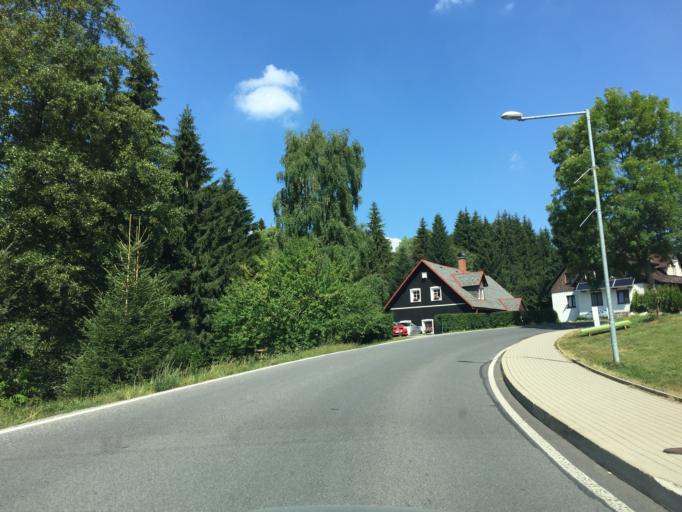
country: CZ
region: Liberecky
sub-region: Okres Jablonec nad Nisou
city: Janov nad Nisou
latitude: 50.7923
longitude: 15.1414
